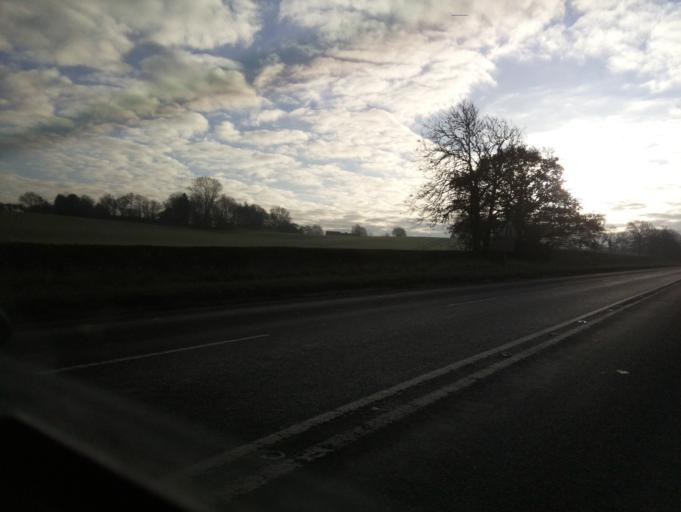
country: GB
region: England
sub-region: Warwickshire
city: Curdworth
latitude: 52.5687
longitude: -1.7625
